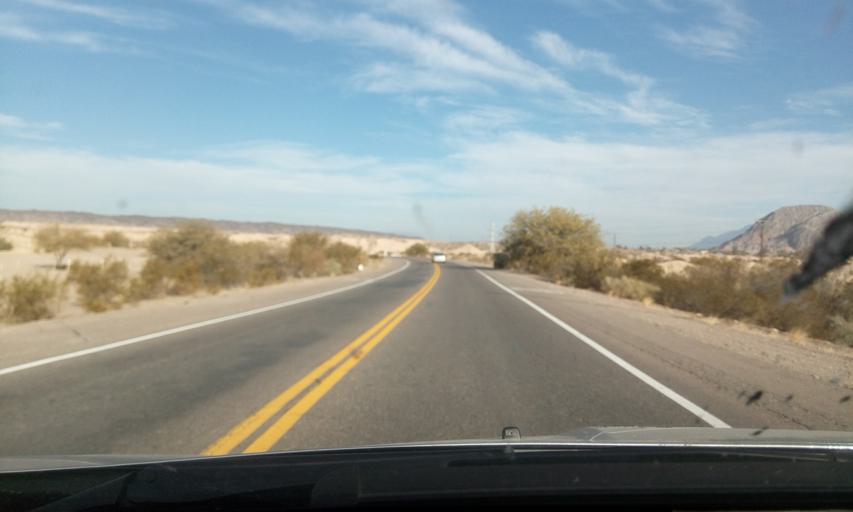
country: AR
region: San Juan
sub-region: Departamento de Rivadavia
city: Rivadavia
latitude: -31.4421
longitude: -68.6533
